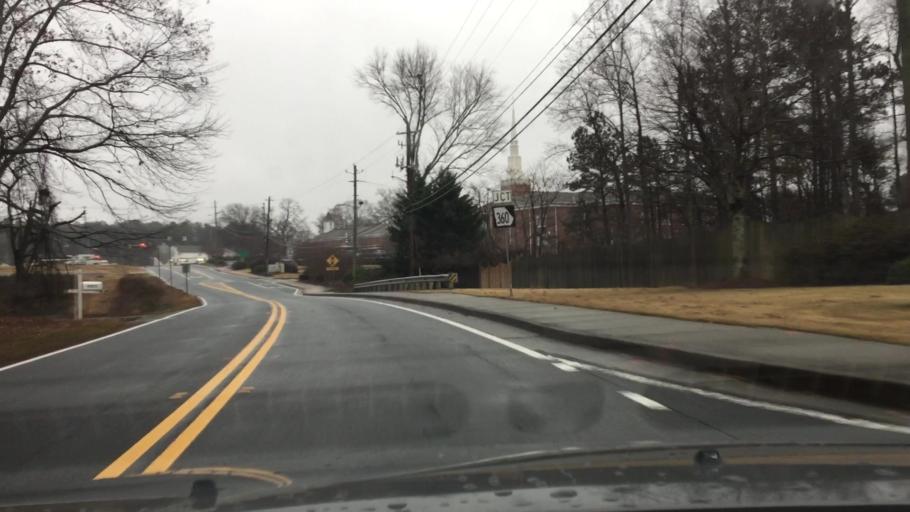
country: US
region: Georgia
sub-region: Cobb County
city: Powder Springs
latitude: 33.9000
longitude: -84.6737
